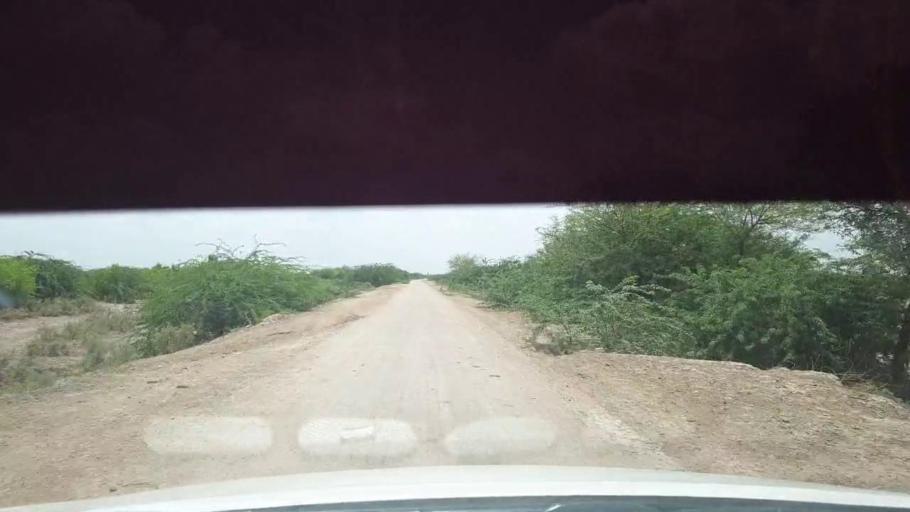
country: PK
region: Sindh
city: Kadhan
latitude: 24.5261
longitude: 69.0914
